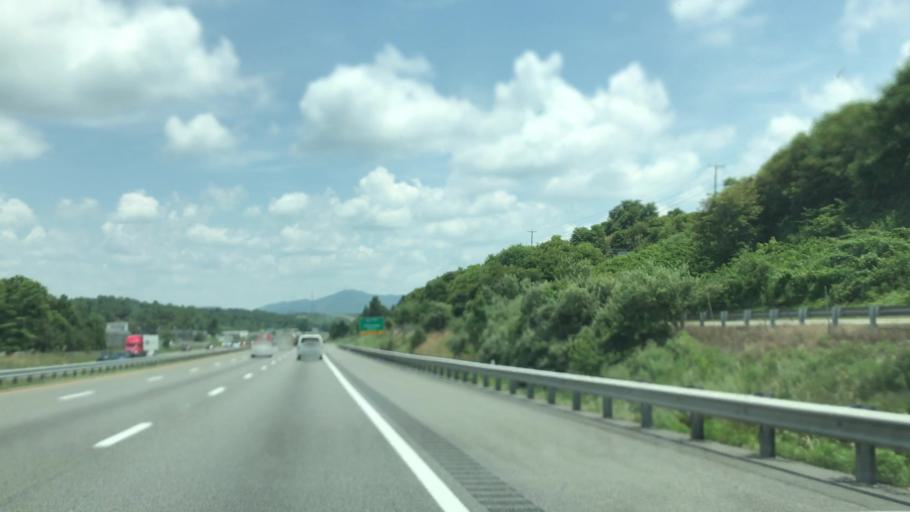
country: US
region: Virginia
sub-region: Wythe County
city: Wytheville
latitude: 36.9387
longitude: -80.9793
